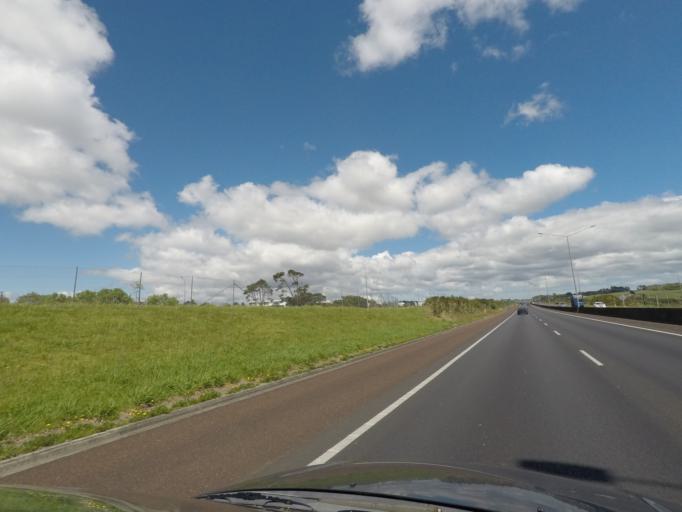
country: NZ
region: Auckland
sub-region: Auckland
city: Rosebank
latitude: -36.7990
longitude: 174.6400
